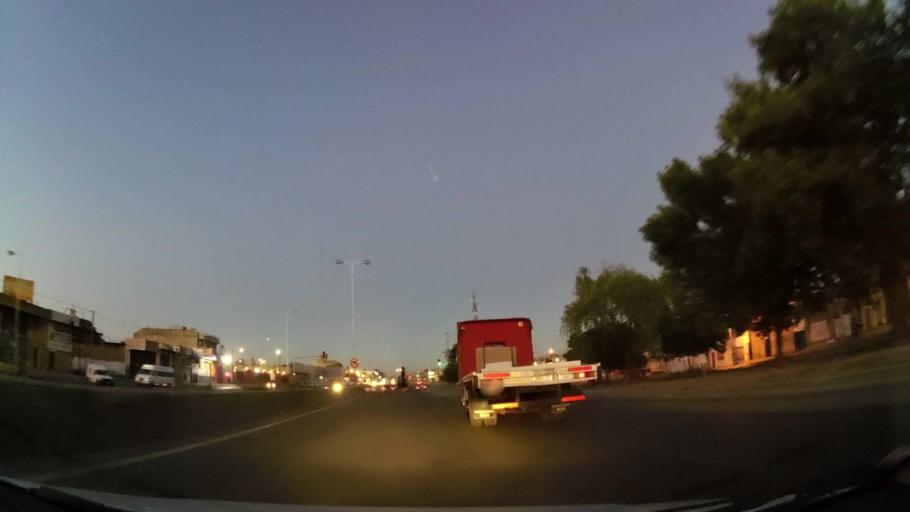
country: AR
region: Buenos Aires
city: San Justo
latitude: -34.7107
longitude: -58.5892
